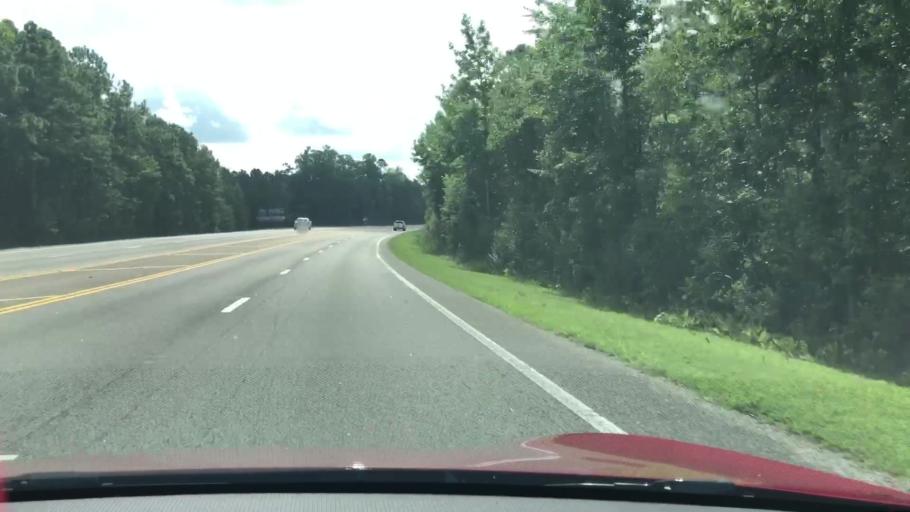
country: US
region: North Carolina
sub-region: Currituck County
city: Currituck
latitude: 36.3366
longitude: -75.9496
